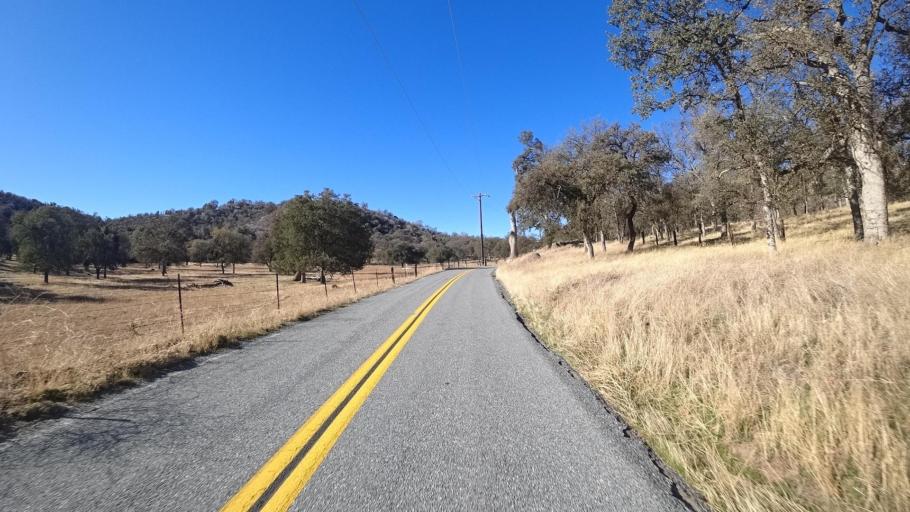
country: US
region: California
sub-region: Kern County
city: Alta Sierra
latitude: 35.7928
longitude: -118.7284
